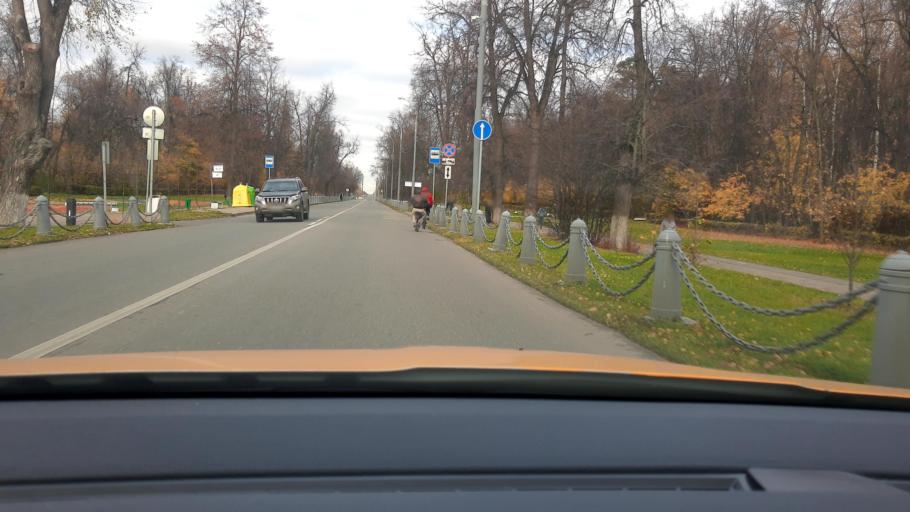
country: RU
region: Moscow
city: Kuz'minki
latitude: 55.6930
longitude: 37.7902
